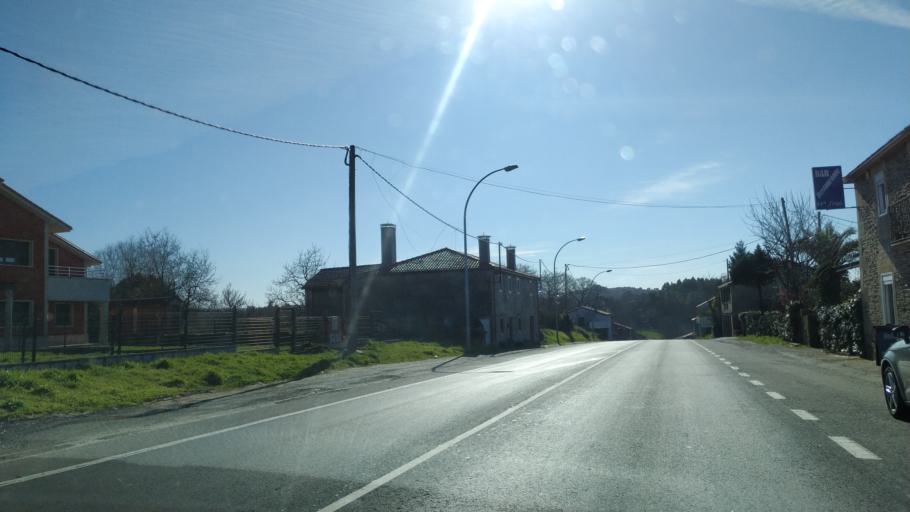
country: ES
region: Galicia
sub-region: Provincia de Pontevedra
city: Lalin
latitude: 42.6789
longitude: -8.1661
